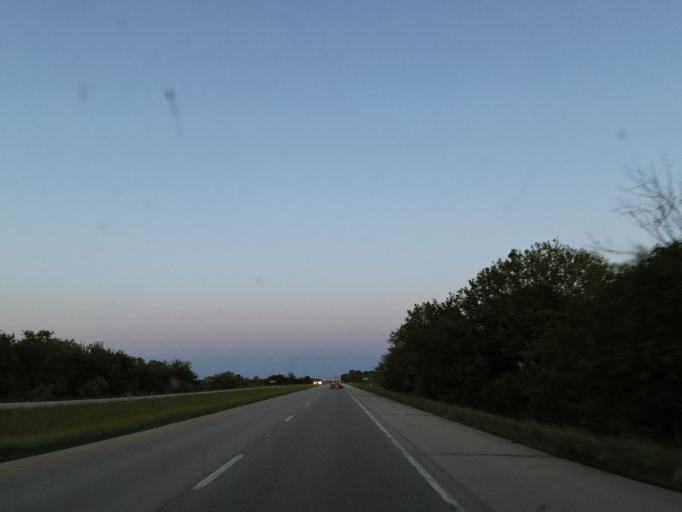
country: US
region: Indiana
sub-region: Boone County
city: Thorntown
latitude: 39.9871
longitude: -86.6986
